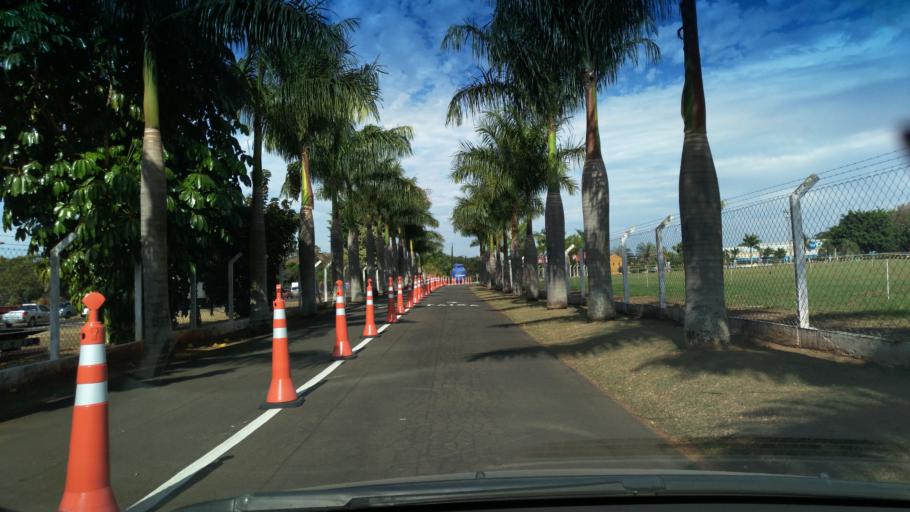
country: BR
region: Sao Paulo
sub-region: Jaguariuna
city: Jaguariuna
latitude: -22.6231
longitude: -47.0592
